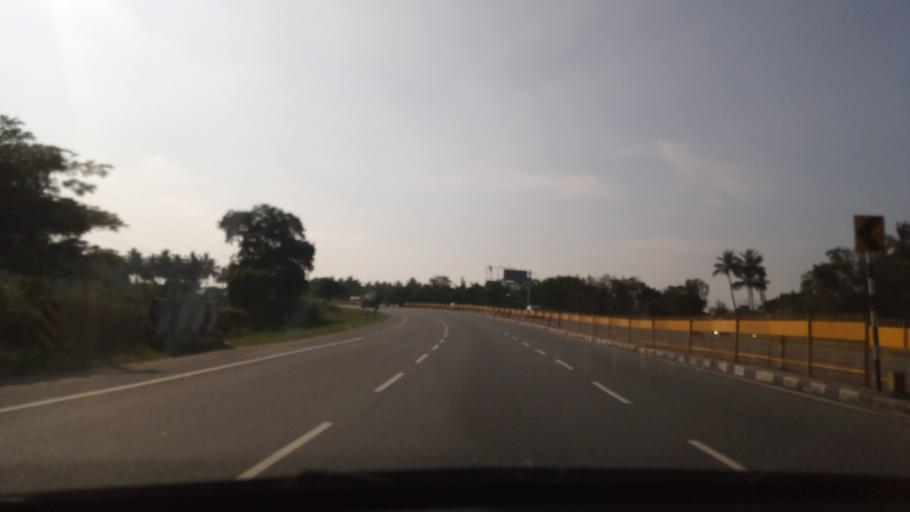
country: IN
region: Tamil Nadu
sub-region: Krishnagiri
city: Krishnagiri
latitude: 12.5477
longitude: 78.3282
